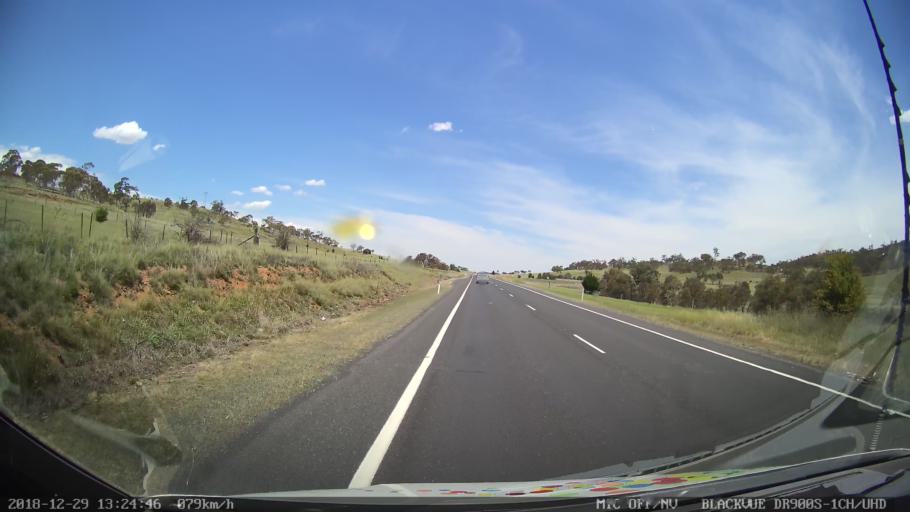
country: AU
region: New South Wales
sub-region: Cooma-Monaro
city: Cooma
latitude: -35.8338
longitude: 149.1622
